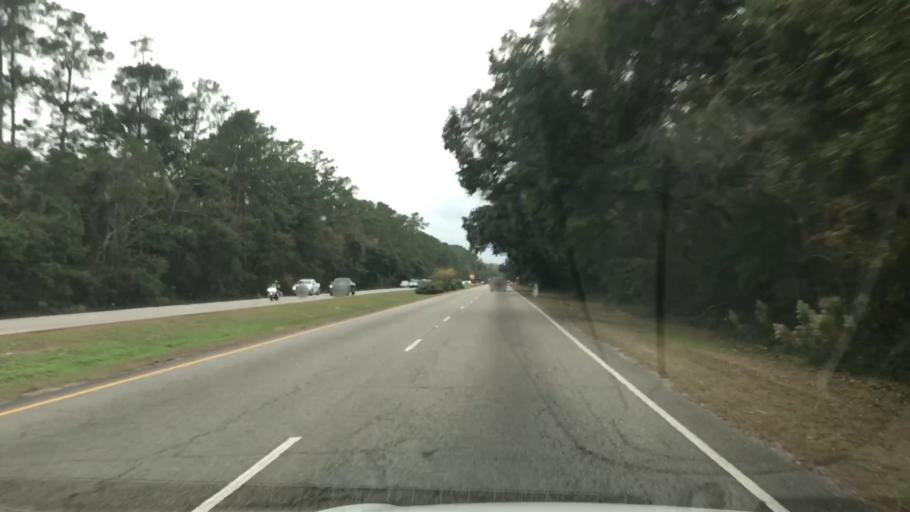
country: US
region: South Carolina
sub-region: Georgetown County
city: Murrells Inlet
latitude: 33.5029
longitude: -79.0814
